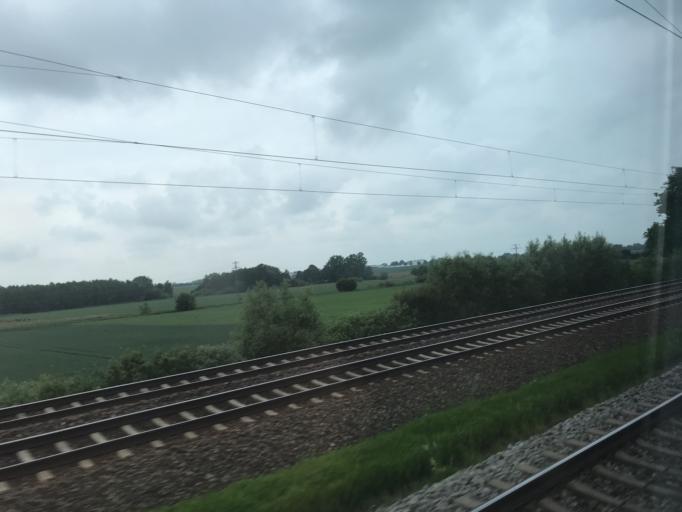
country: DE
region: Bavaria
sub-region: Swabia
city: Merching
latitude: 48.2515
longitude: 11.0104
